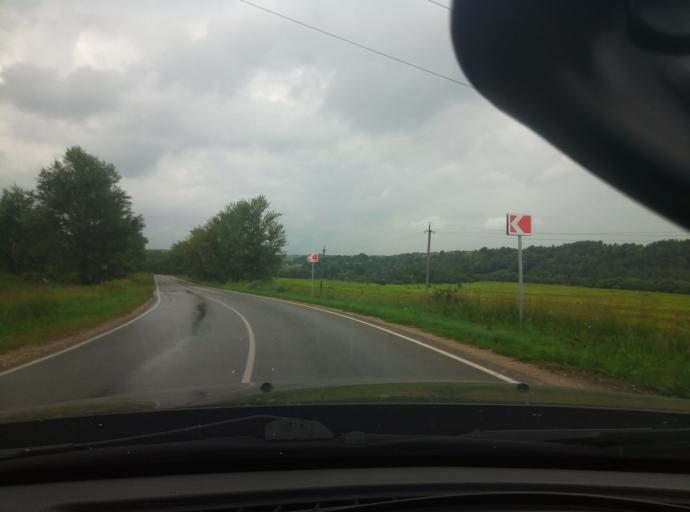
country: RU
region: Tula
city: Lomintsevskiy
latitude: 53.9655
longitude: 37.6601
